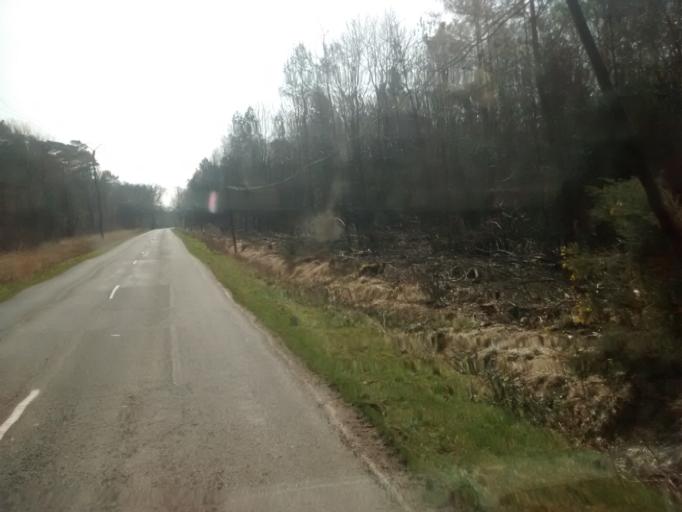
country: FR
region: Brittany
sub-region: Departement d'Ille-et-Vilaine
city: Paimpont
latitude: 48.0287
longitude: -2.1753
